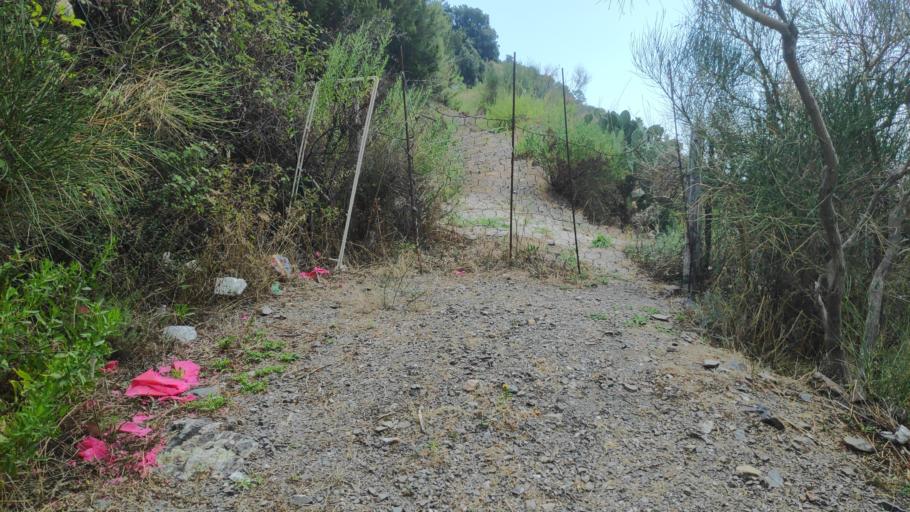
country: IT
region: Calabria
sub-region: Provincia di Reggio Calabria
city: Bivongi
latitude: 38.4949
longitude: 16.4456
